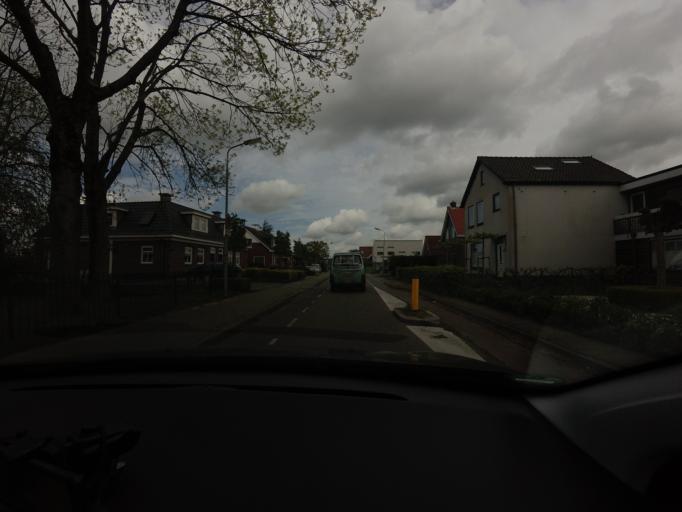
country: NL
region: North Holland
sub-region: Gemeente Zaanstad
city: Zaandam
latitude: 52.4537
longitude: 4.8685
